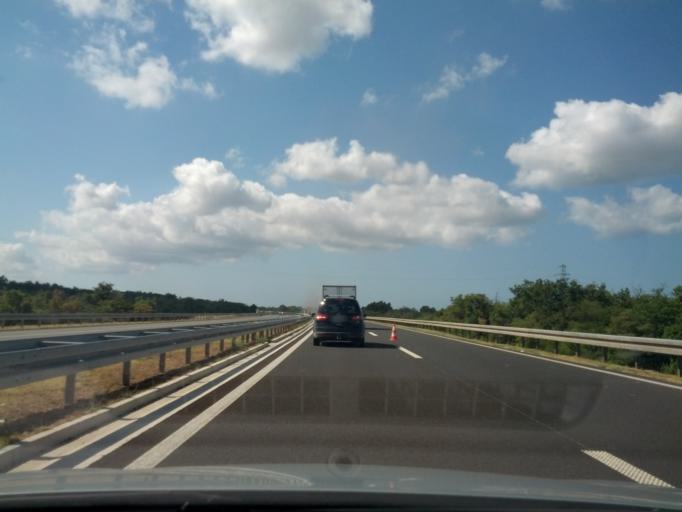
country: HR
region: Istarska
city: Vodnjan
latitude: 45.0107
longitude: 13.8382
